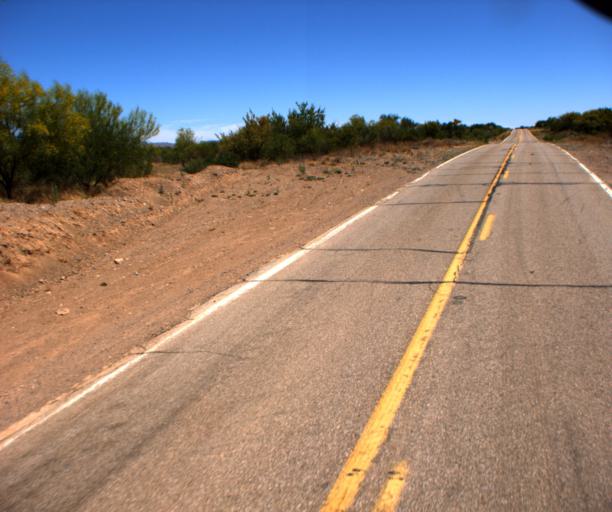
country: US
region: Arizona
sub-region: Pima County
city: Arivaca Junction
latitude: 31.6813
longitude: -111.4862
